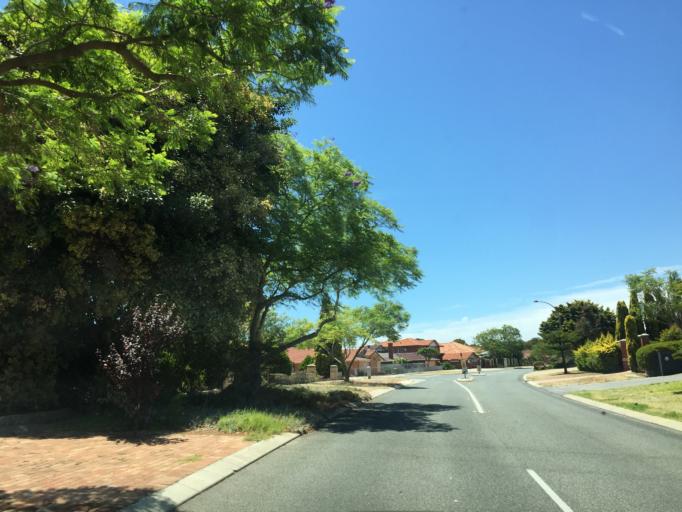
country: AU
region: Western Australia
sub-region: Melville
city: Winthrop
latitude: -32.0615
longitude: 115.8355
